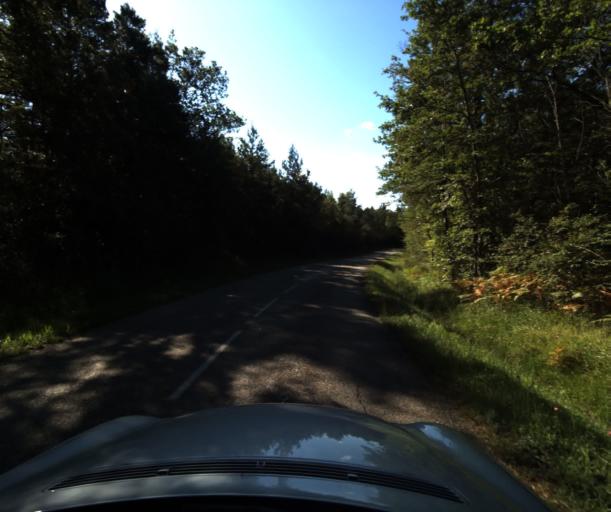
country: FR
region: Languedoc-Roussillon
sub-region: Departement de l'Aude
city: Chalabre
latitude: 42.9670
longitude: 1.9886
